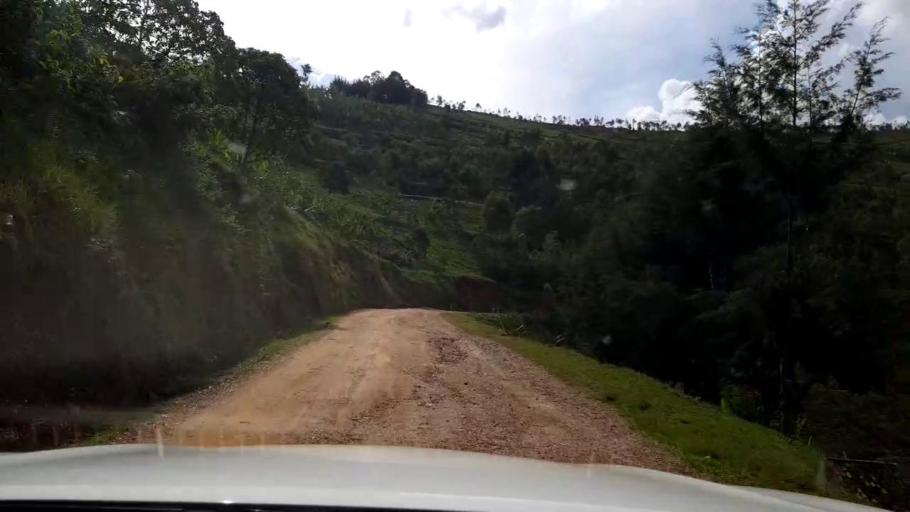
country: RW
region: Southern Province
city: Gitarama
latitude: -1.9953
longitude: 29.7091
